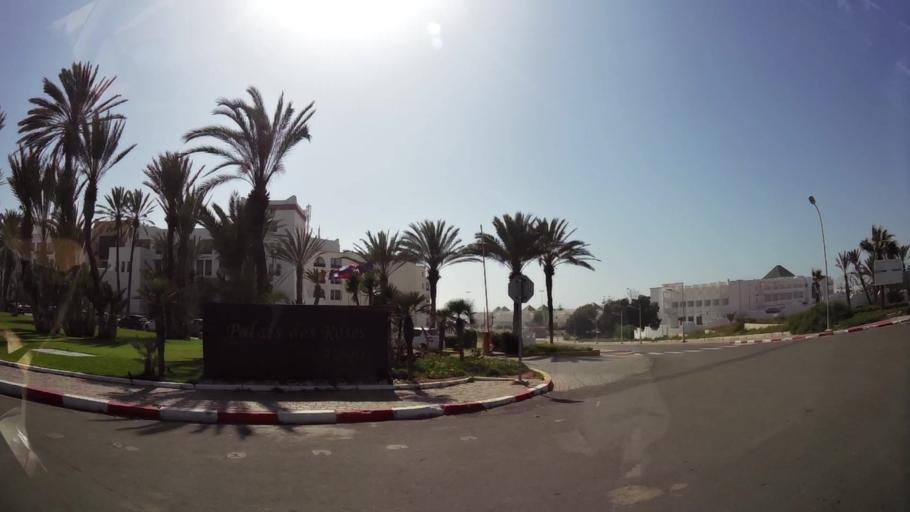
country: MA
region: Souss-Massa-Draa
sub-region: Agadir-Ida-ou-Tnan
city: Agadir
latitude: 30.3956
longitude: -9.5958
